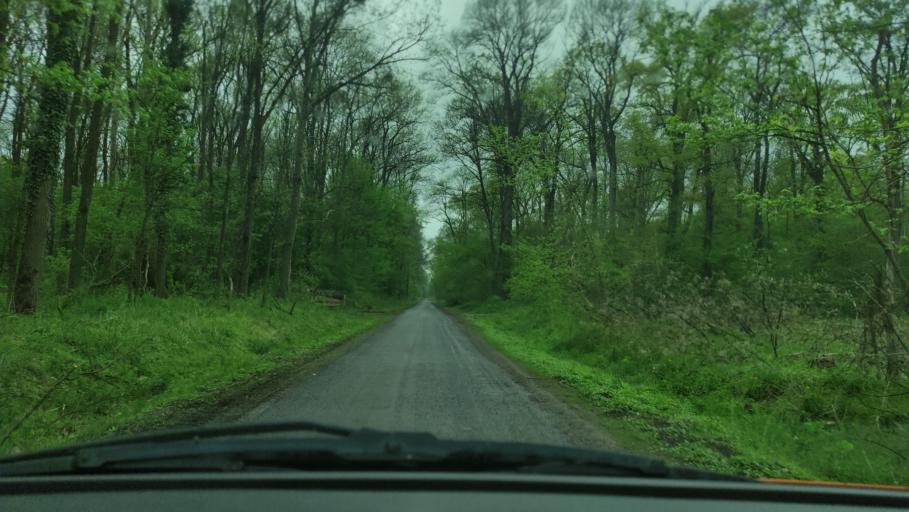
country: HU
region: Baranya
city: Mohacs
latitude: 45.9109
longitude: 18.7419
